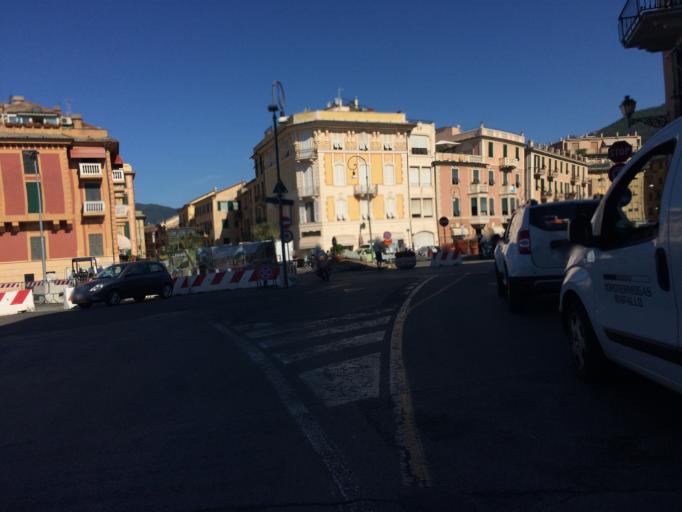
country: IT
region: Liguria
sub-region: Provincia di Genova
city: Rapallo
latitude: 44.3484
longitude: 9.2343
